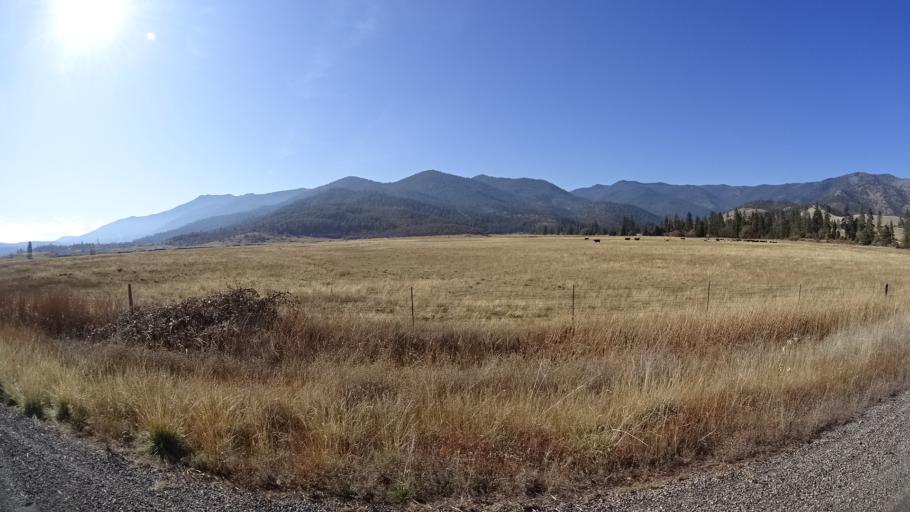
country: US
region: California
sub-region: Siskiyou County
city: Weed
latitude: 41.4468
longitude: -122.4465
